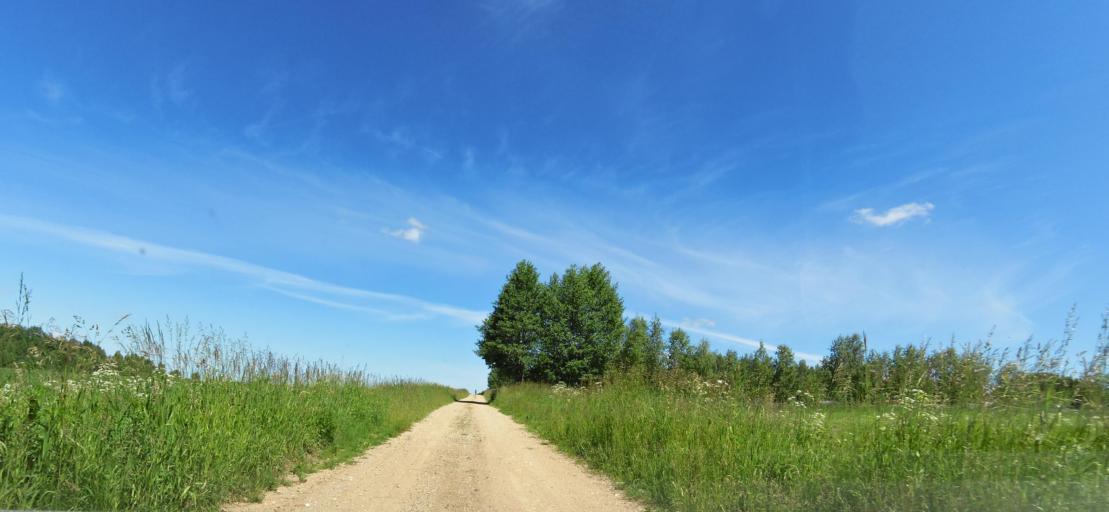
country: LT
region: Vilnius County
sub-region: Vilnius
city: Fabijoniskes
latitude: 55.0132
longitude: 25.2429
